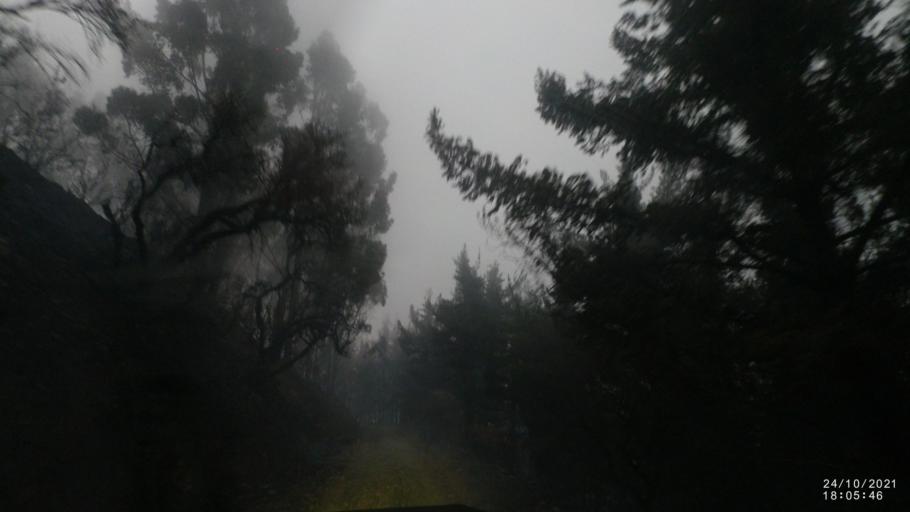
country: BO
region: Cochabamba
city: Cochabamba
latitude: -17.3255
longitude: -66.1336
